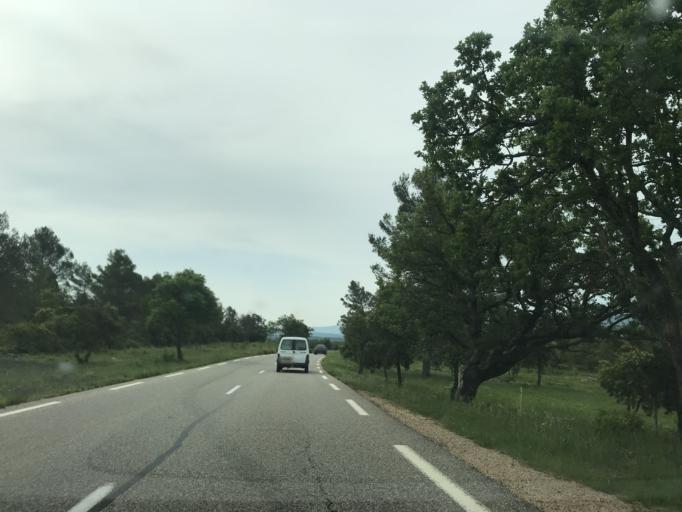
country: FR
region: Provence-Alpes-Cote d'Azur
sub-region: Departement du Var
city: Pourrieres
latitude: 43.5025
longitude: 5.8061
